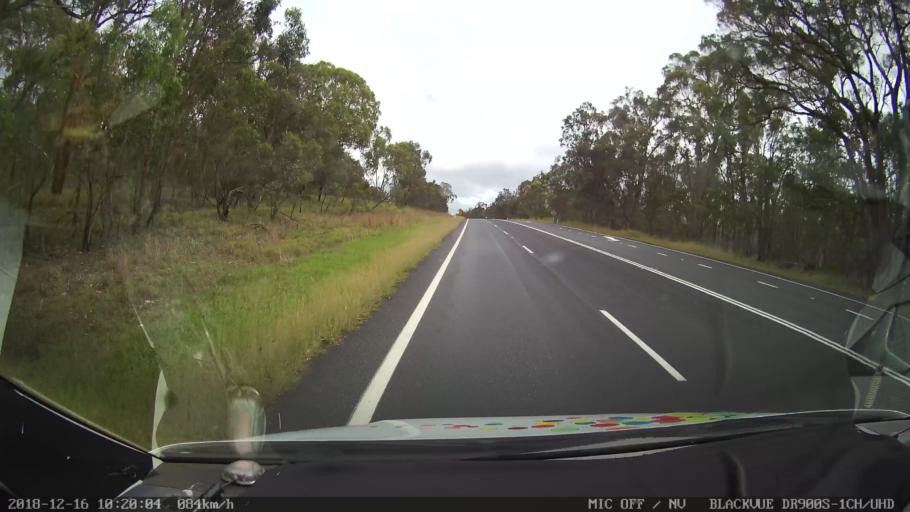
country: AU
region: New South Wales
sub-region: Tenterfield Municipality
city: Carrolls Creek
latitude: -29.2249
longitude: 152.0094
